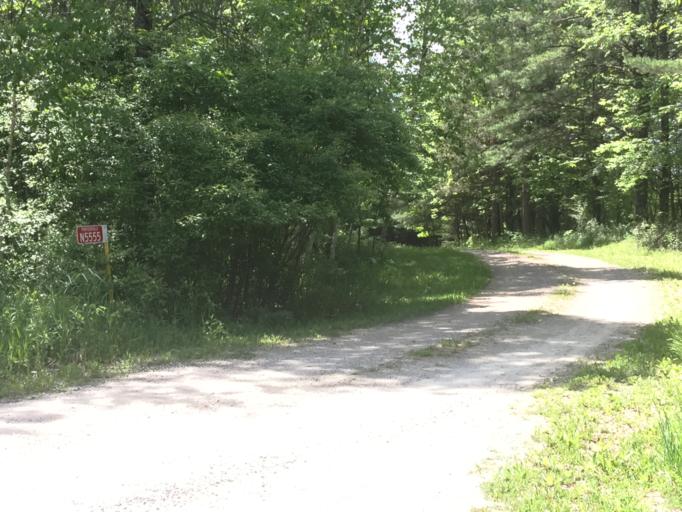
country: US
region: Wisconsin
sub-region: Marinette County
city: Peshtigo
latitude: 45.1591
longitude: -87.7799
